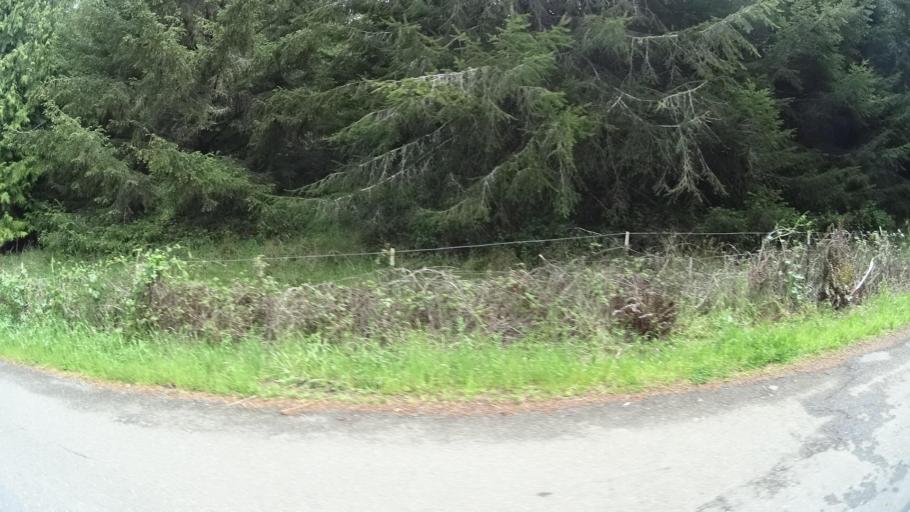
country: US
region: California
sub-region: Humboldt County
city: Bayside
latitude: 40.8339
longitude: -124.0138
